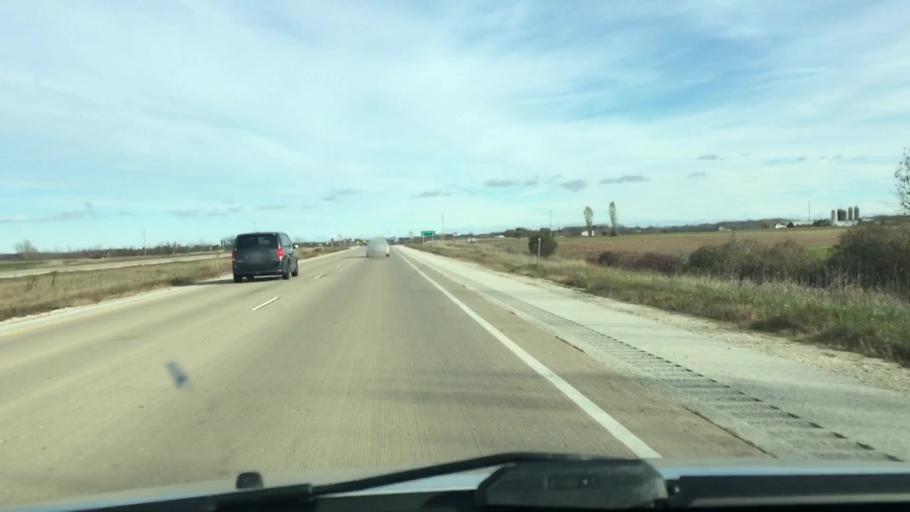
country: US
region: Wisconsin
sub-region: Kewaunee County
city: Luxemburg
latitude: 44.7161
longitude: -87.6549
